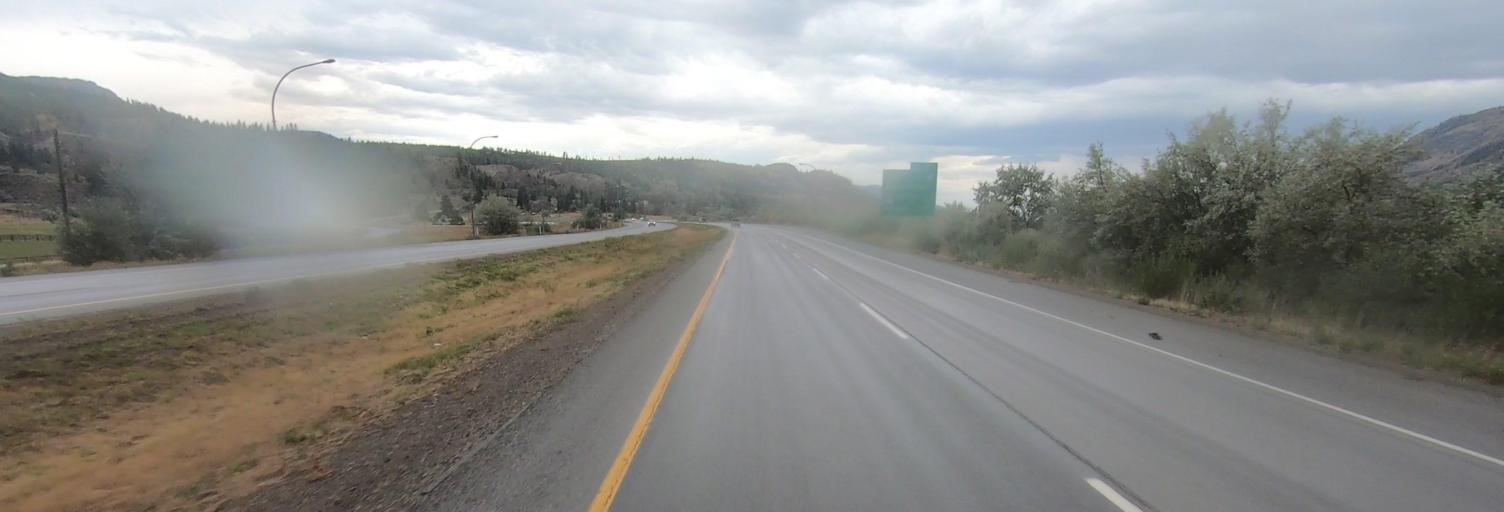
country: CA
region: British Columbia
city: Chase
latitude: 50.6493
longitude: -119.9760
